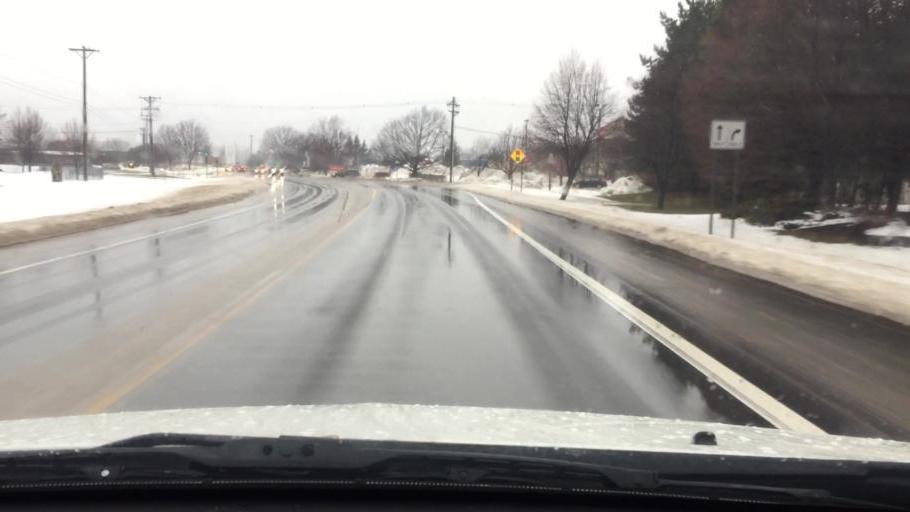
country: US
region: Michigan
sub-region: Charlevoix County
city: Charlevoix
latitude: 45.3014
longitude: -85.2575
